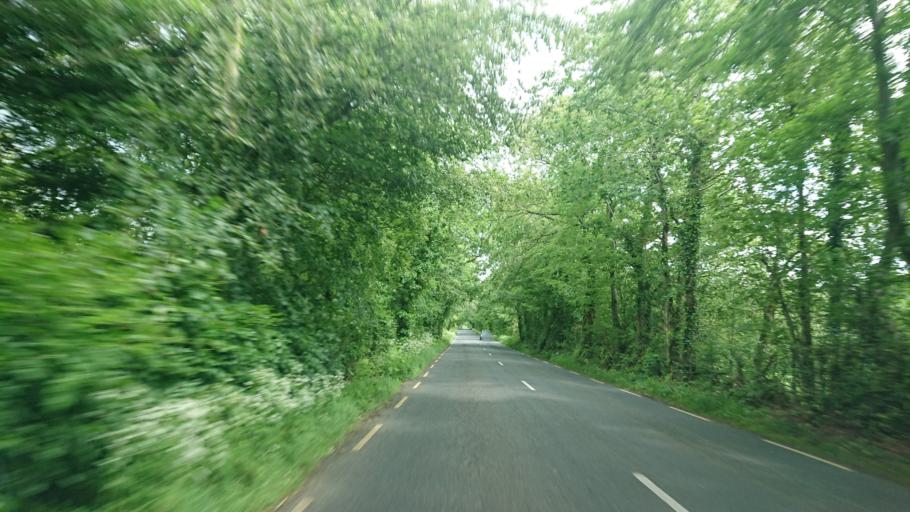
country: IE
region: Leinster
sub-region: Kilkenny
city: Graiguenamanagh
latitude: 52.4783
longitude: -6.9501
